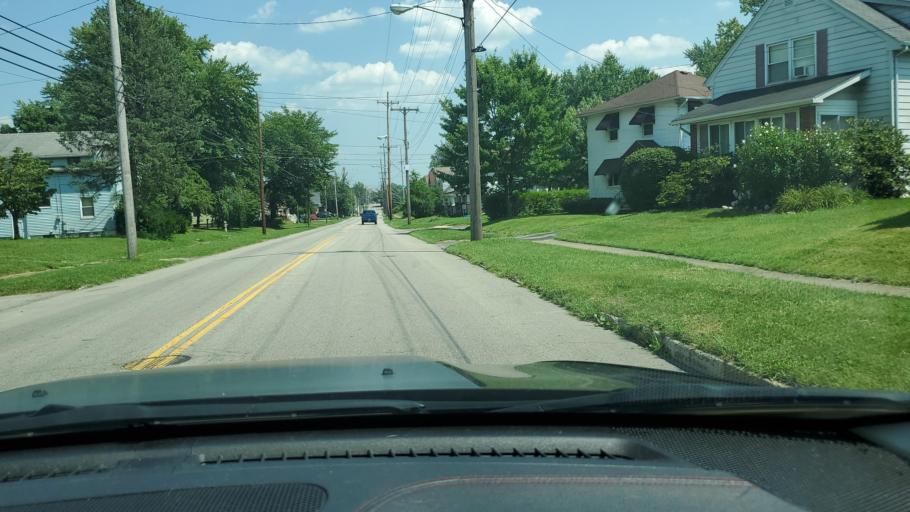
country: US
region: Ohio
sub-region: Trumbull County
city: Niles
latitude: 41.1844
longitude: -80.7794
